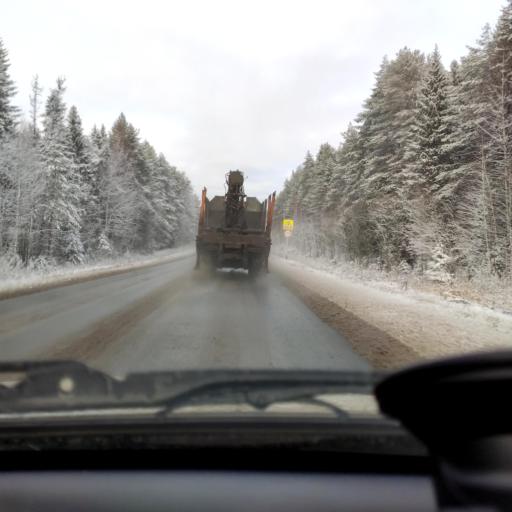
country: RU
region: Perm
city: Nytva
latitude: 57.9751
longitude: 55.3658
